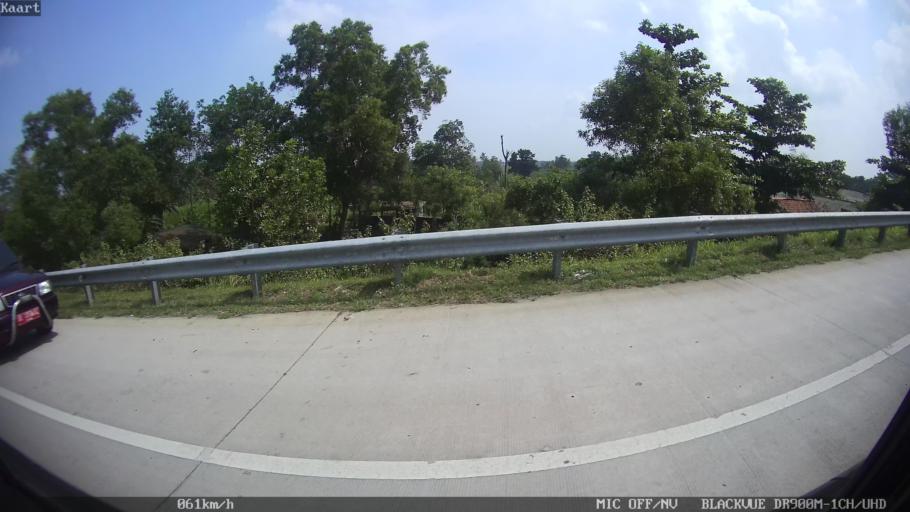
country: ID
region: Lampung
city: Natar
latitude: -5.2812
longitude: 105.1971
